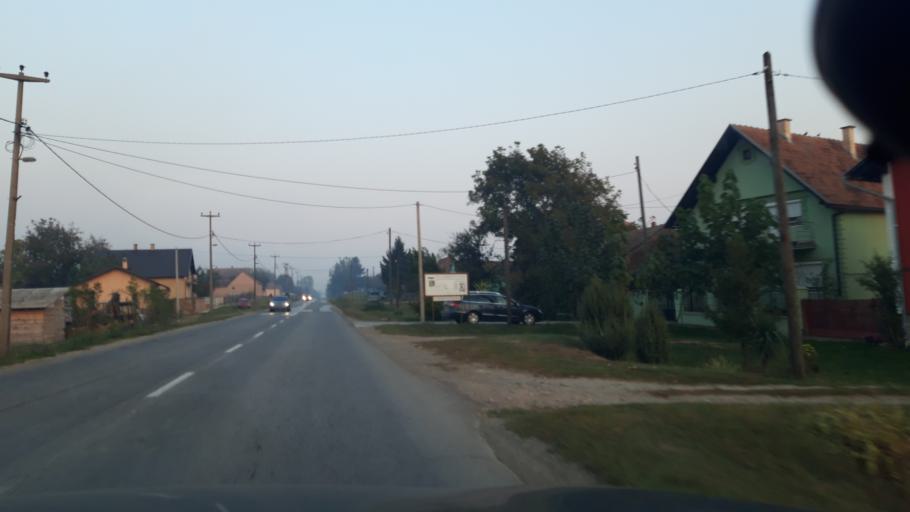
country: RS
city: Putinci
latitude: 45.0027
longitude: 19.9280
